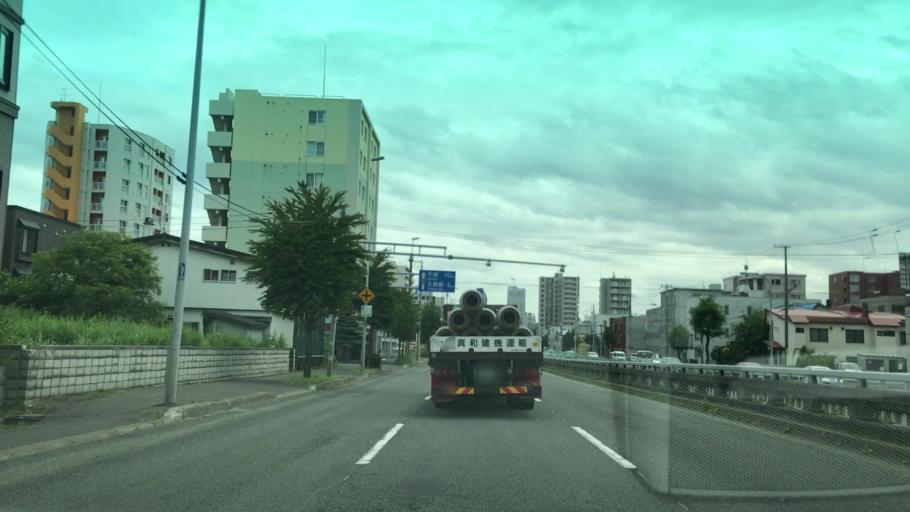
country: JP
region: Hokkaido
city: Sapporo
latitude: 43.0905
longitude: 141.3479
